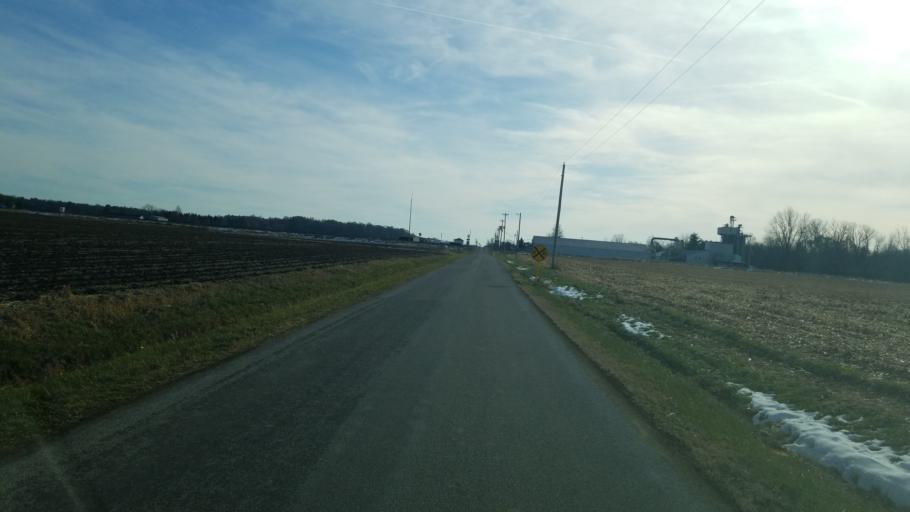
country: US
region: Ohio
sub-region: Huron County
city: New London
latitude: 41.0351
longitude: -82.2803
